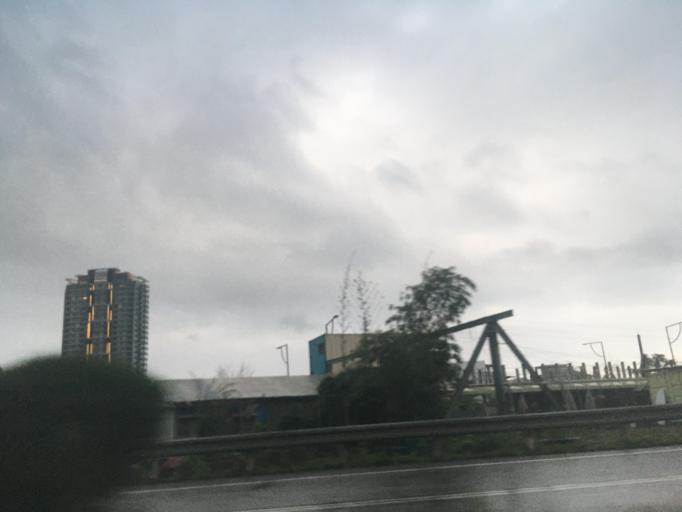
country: TW
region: Taiwan
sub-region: Yilan
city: Yilan
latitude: 24.8638
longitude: 121.8287
